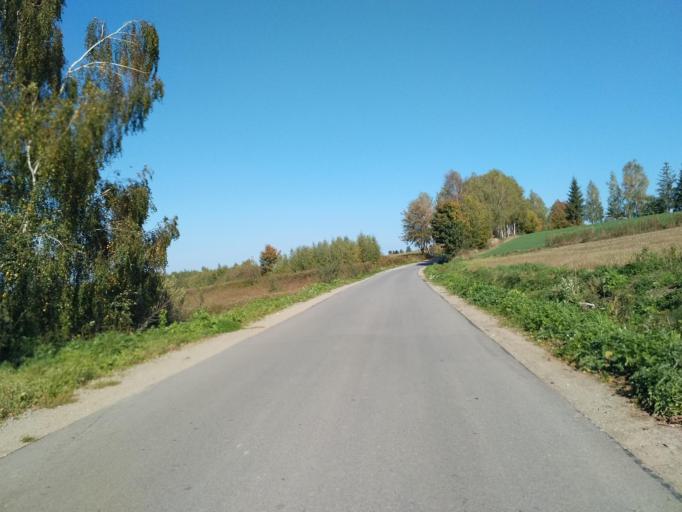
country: PL
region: Subcarpathian Voivodeship
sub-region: Powiat debicki
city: Brzostek
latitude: 49.9540
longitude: 21.3869
